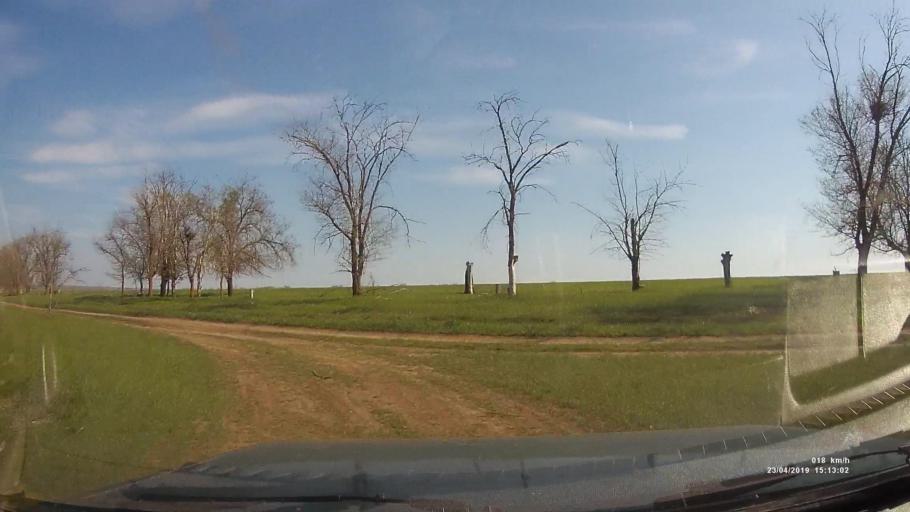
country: RU
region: Rostov
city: Remontnoye
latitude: 46.5400
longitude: 42.9535
